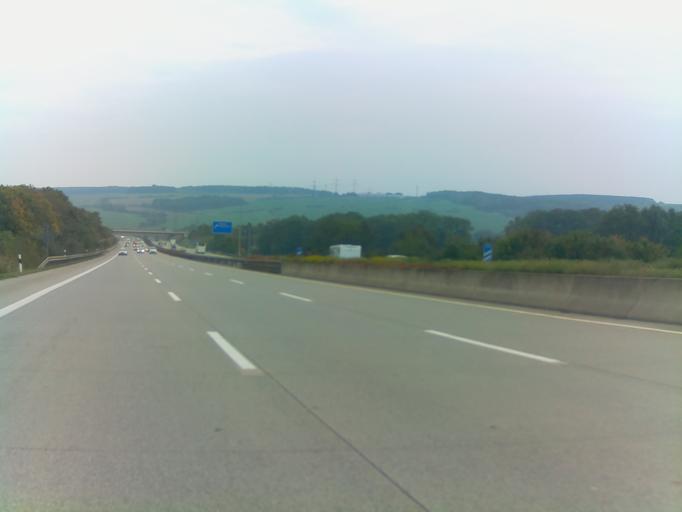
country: DE
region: Thuringia
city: Magdala
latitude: 50.9012
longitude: 11.4321
